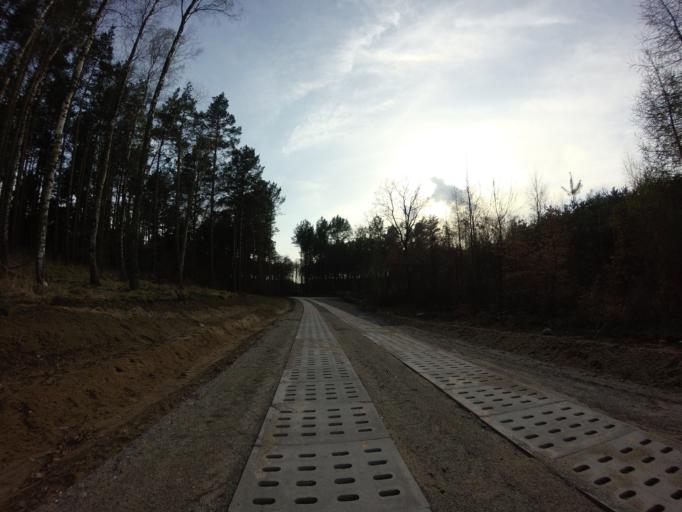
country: PL
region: West Pomeranian Voivodeship
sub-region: Powiat choszczenski
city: Recz
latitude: 53.1936
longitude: 15.5279
